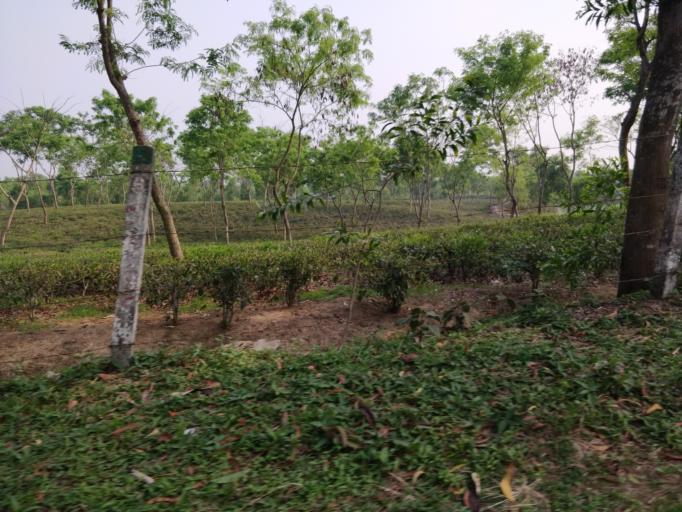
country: IN
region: Tripura
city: Khowai
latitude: 24.1304
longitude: 91.3853
